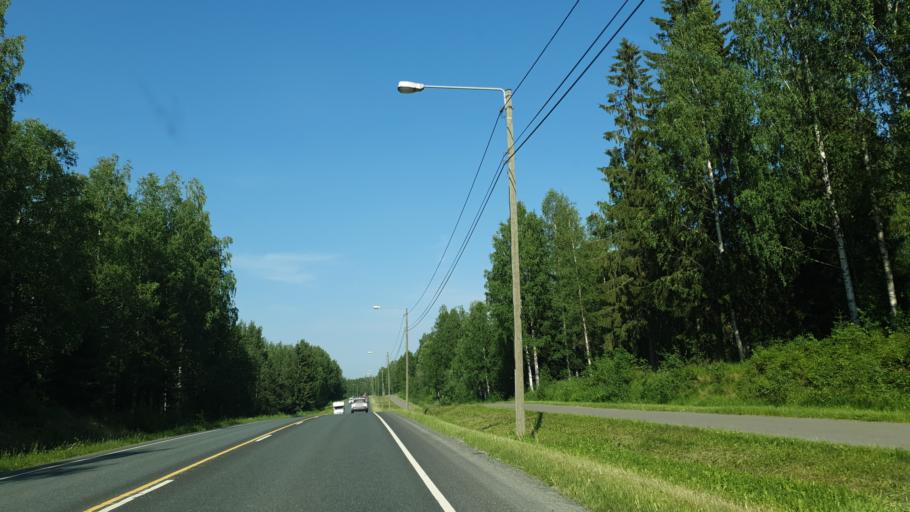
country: FI
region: Northern Savo
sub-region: Kuopio
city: Siilinjaervi
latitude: 63.0891
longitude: 27.7130
